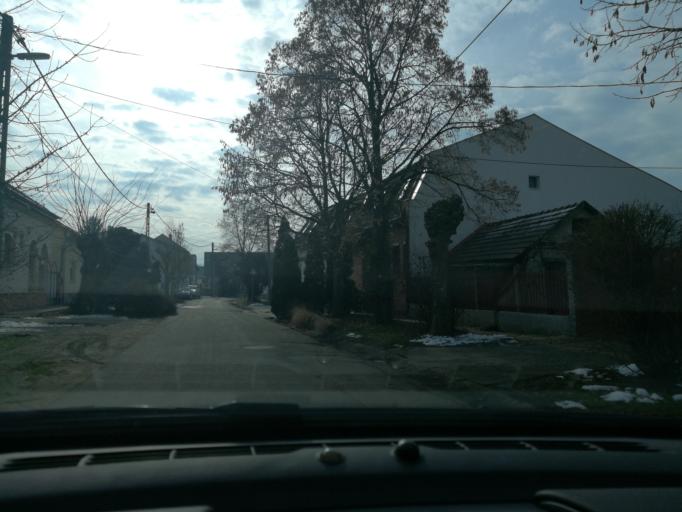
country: HU
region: Szabolcs-Szatmar-Bereg
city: Nyiregyhaza
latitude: 47.9464
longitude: 21.7217
